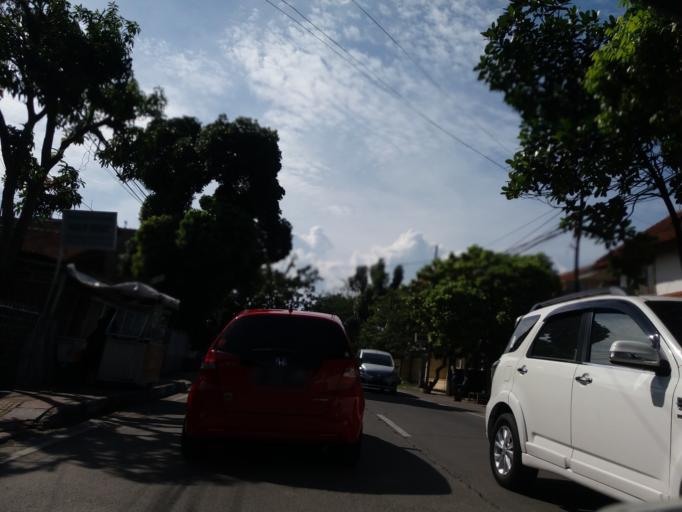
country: ID
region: West Java
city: Bandung
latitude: -6.9417
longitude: 107.6128
